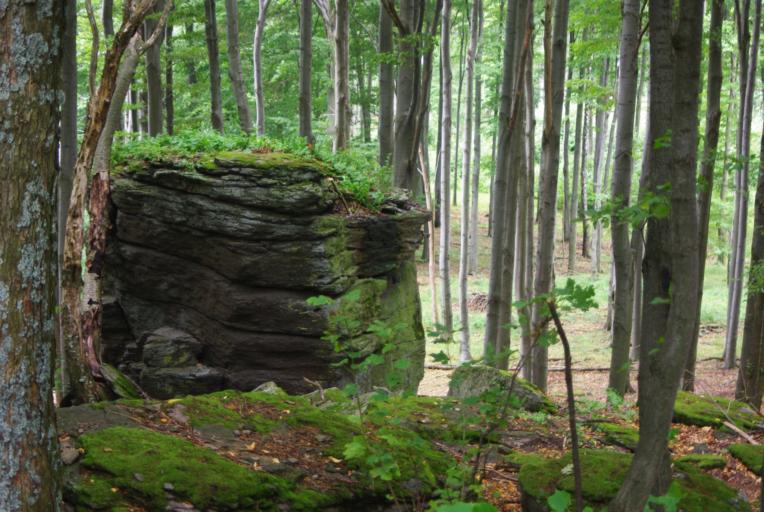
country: HU
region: Borsod-Abauj-Zemplen
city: Gonc
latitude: 48.4150
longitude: 21.3792
